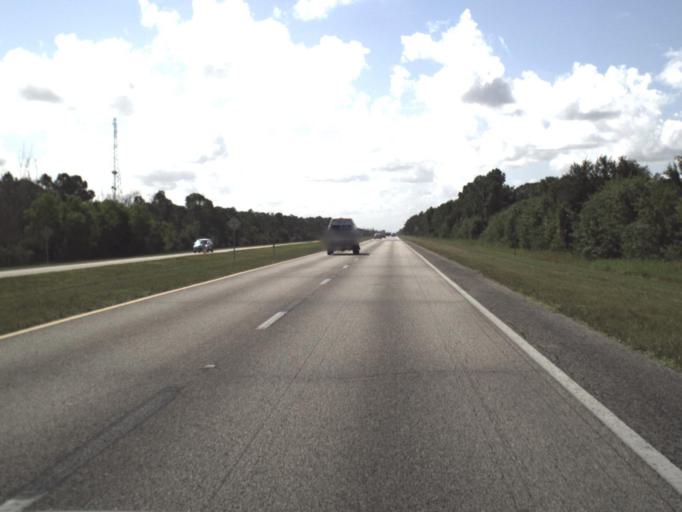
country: US
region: Florida
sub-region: Lee County
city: Burnt Store Marina
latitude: 26.8341
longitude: -81.9725
